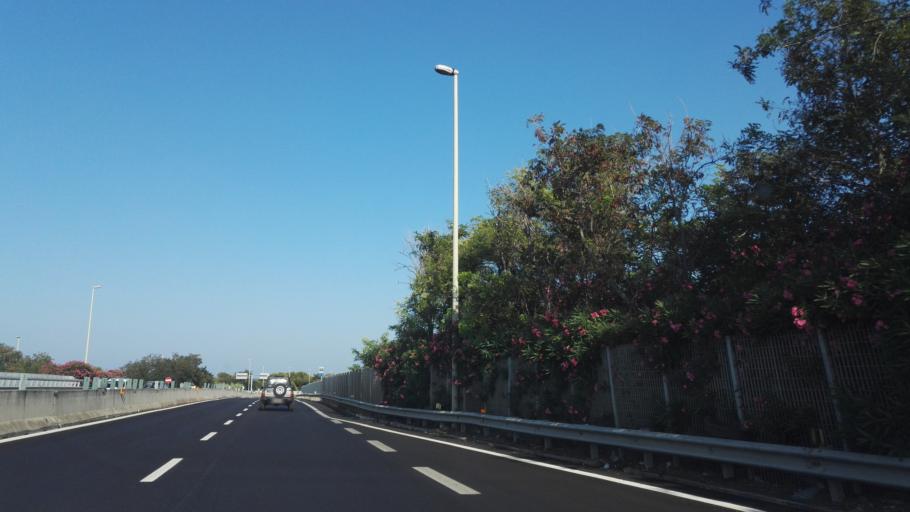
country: IT
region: Apulia
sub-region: Provincia di Bari
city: Mola di Bari
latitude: 41.0329
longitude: 17.1406
